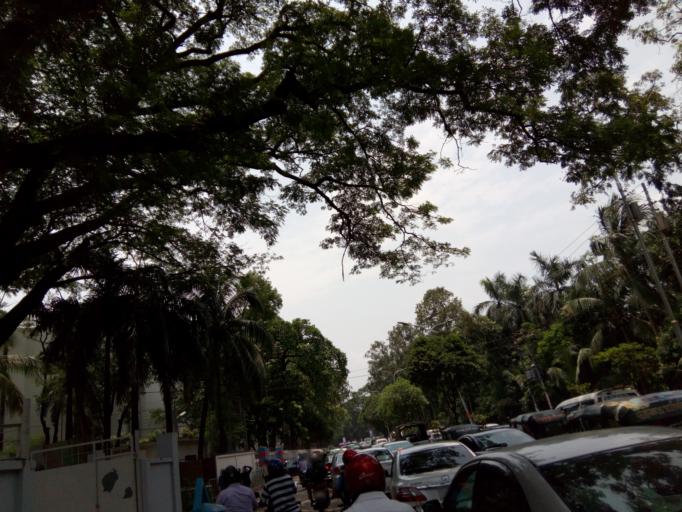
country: BD
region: Dhaka
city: Paltan
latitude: 23.7354
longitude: 90.4039
